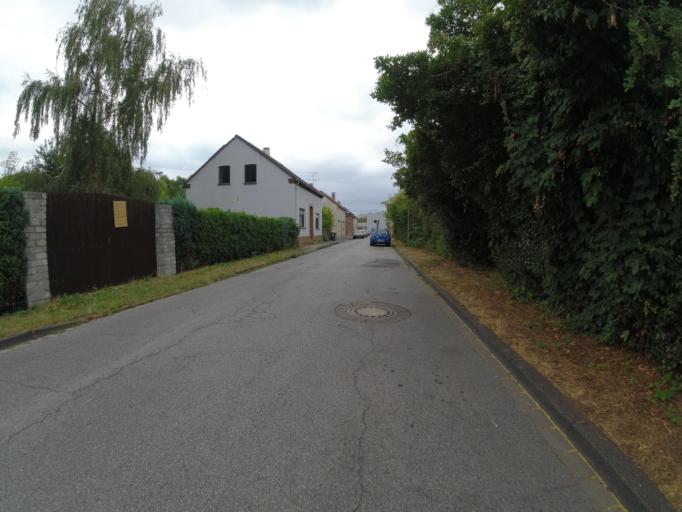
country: DE
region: North Rhine-Westphalia
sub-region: Regierungsbezirk Dusseldorf
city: Hochfeld
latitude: 51.4429
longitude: 6.7042
